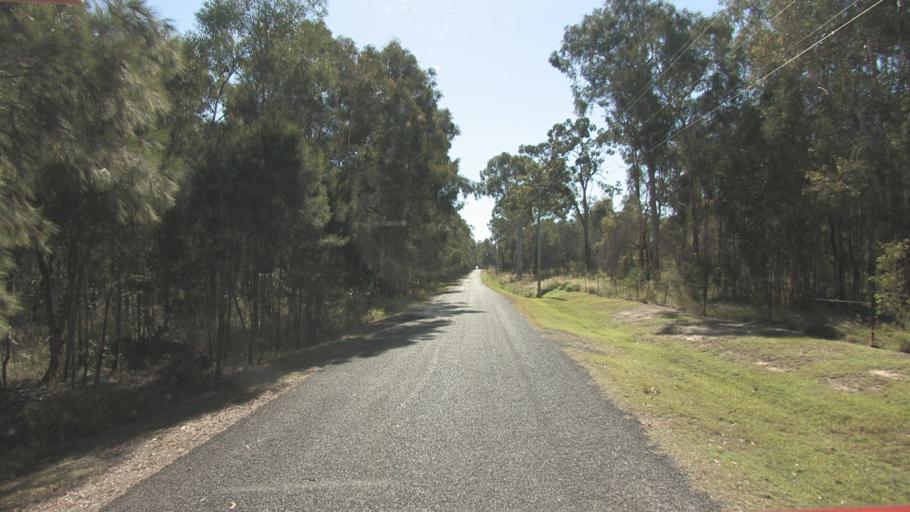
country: AU
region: Queensland
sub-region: Logan
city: Park Ridge South
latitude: -27.6912
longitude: 153.0054
